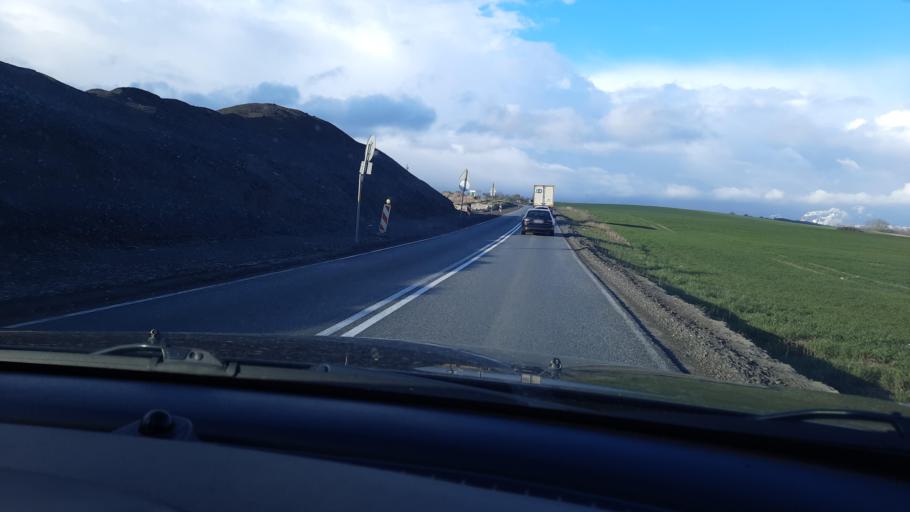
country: PL
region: Kujawsko-Pomorskie
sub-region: Powiat swiecki
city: Pruszcz
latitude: 53.3405
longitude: 18.2972
